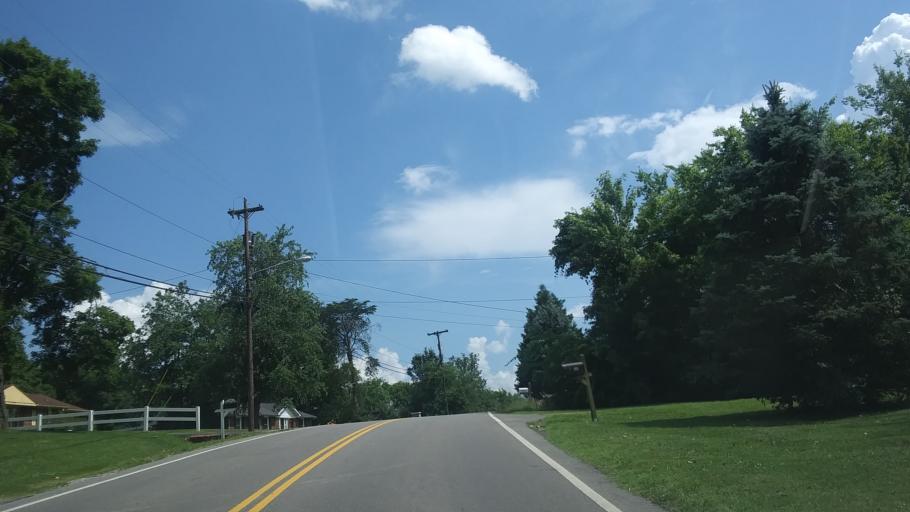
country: US
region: Tennessee
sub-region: Davidson County
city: Oak Hill
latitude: 36.0785
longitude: -86.7028
